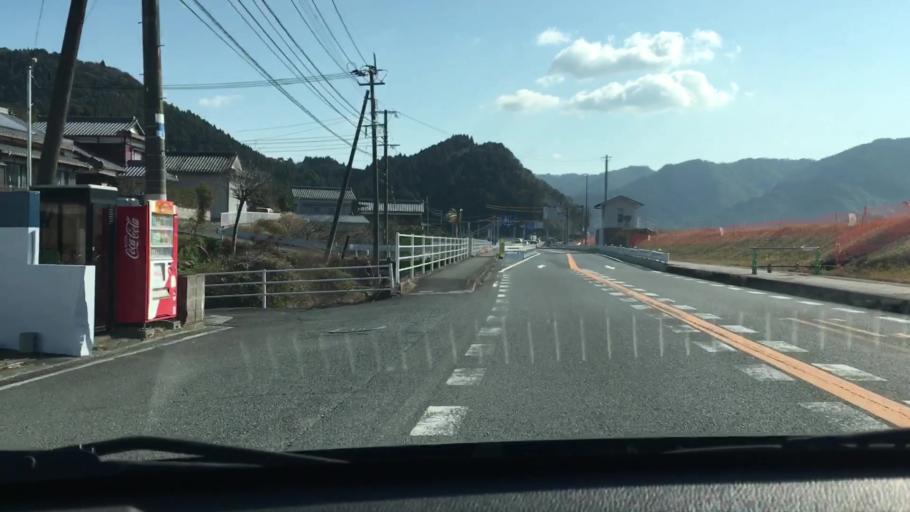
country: JP
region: Oita
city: Saiki
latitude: 32.9597
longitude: 131.8419
